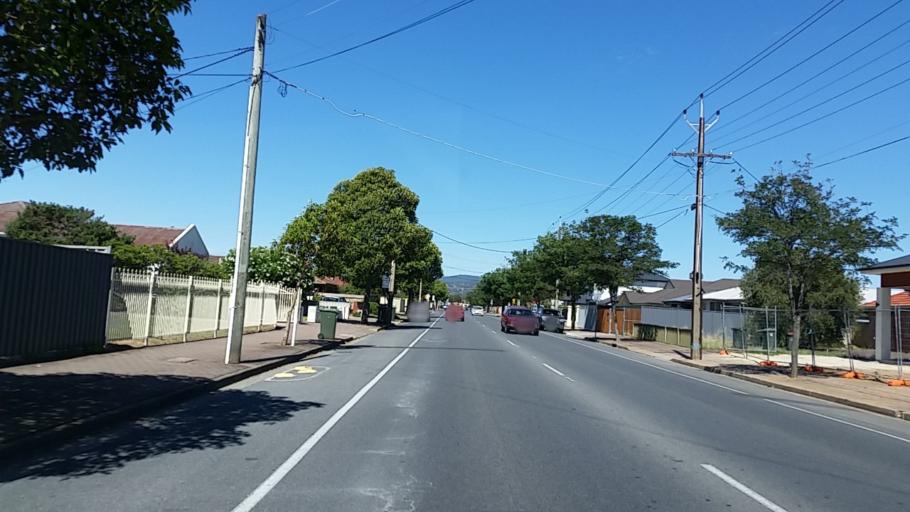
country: AU
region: South Australia
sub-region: Marion
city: South Plympton
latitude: -34.9804
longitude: 138.5589
